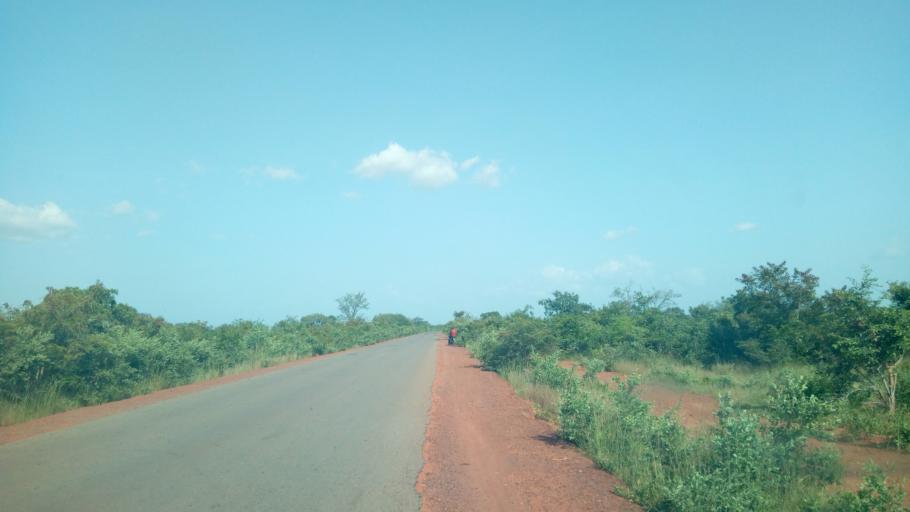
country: ML
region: Sikasso
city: Yorosso
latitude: 12.2122
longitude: -4.9070
